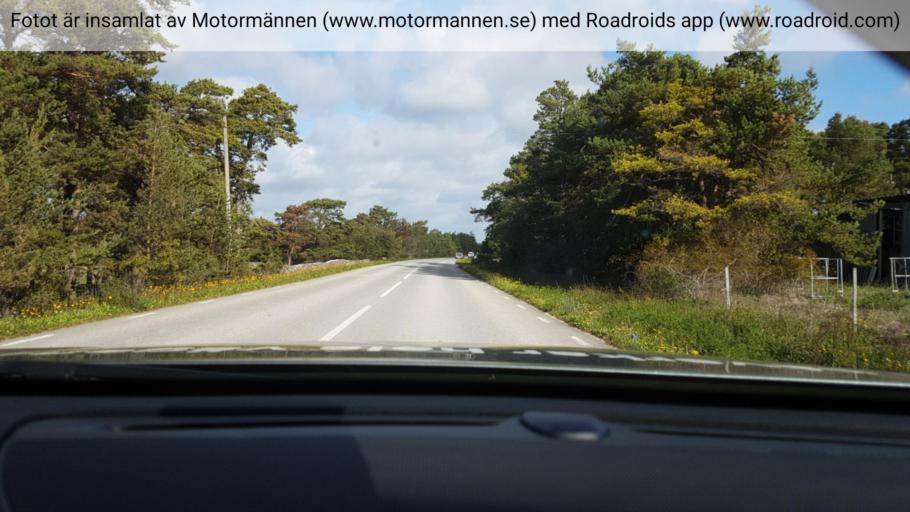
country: SE
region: Gotland
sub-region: Gotland
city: Slite
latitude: 57.8788
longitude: 19.0869
